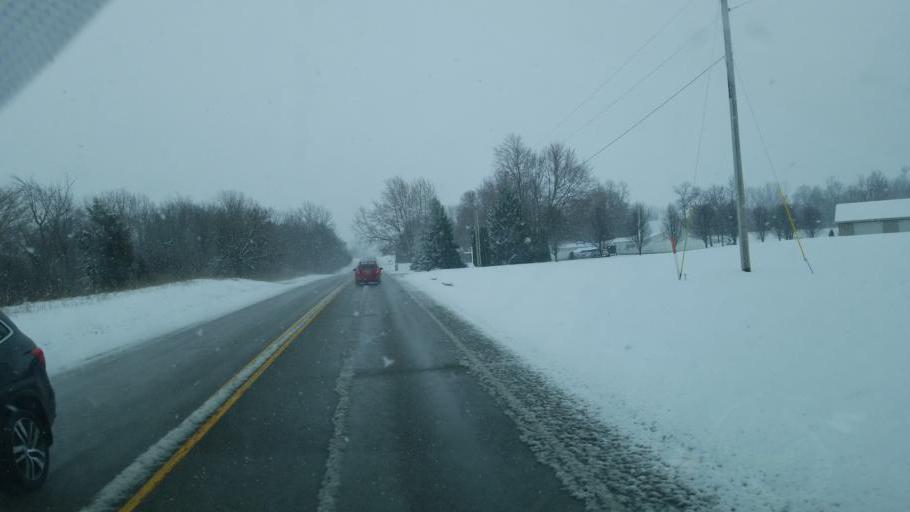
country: US
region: Indiana
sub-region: Randolph County
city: Parker City
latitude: 40.0507
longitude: -85.2227
